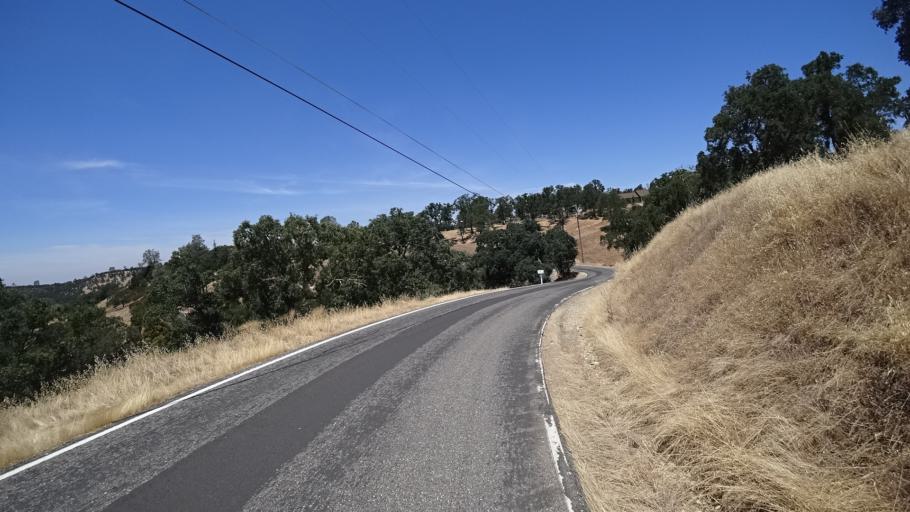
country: US
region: California
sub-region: Calaveras County
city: Rancho Calaveras
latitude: 38.1360
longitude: -120.8595
